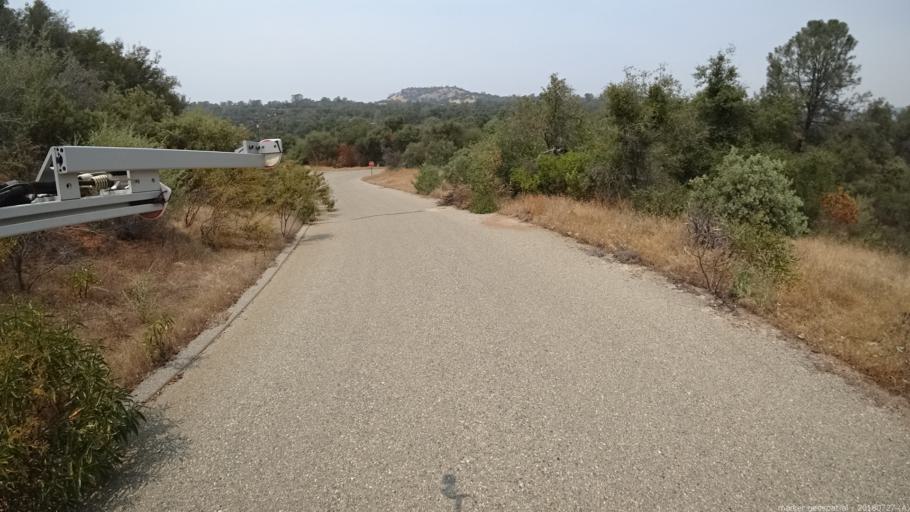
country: US
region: California
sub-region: Madera County
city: Coarsegold
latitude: 37.2481
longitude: -119.7103
